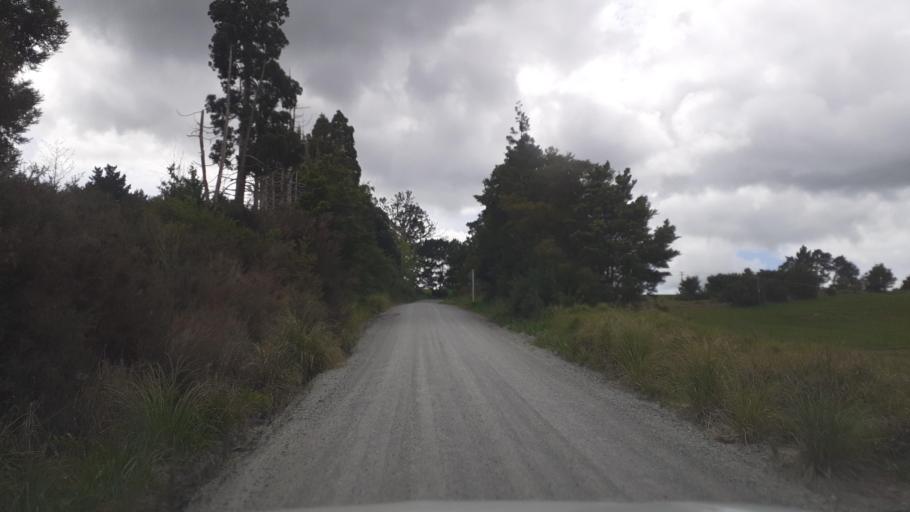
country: NZ
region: Northland
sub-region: Far North District
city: Moerewa
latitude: -35.3883
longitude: 173.9972
